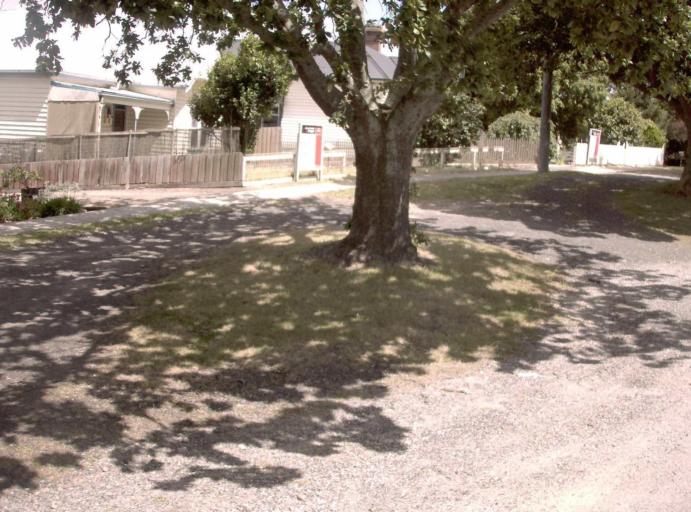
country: AU
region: Victoria
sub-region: Bass Coast
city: North Wonthaggi
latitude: -38.4253
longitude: 145.8199
